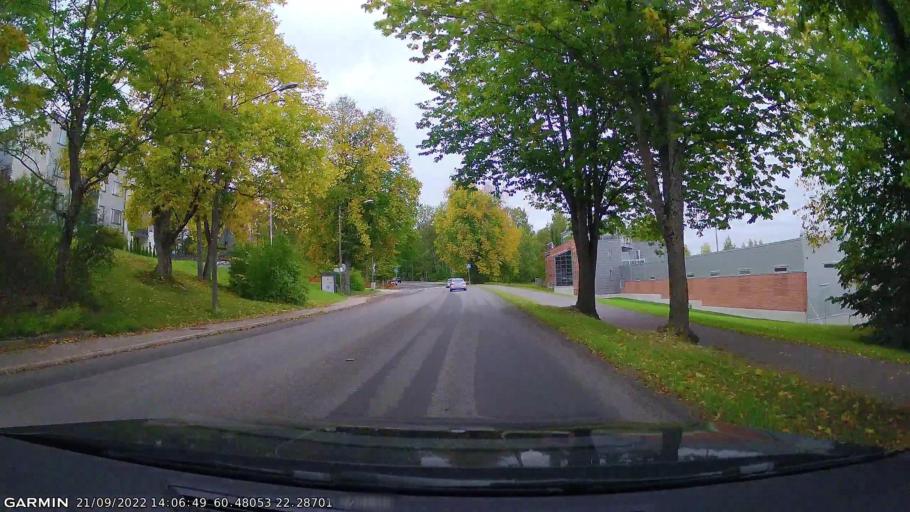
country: FI
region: Varsinais-Suomi
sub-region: Turku
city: Turku
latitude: 60.4805
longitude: 22.2869
